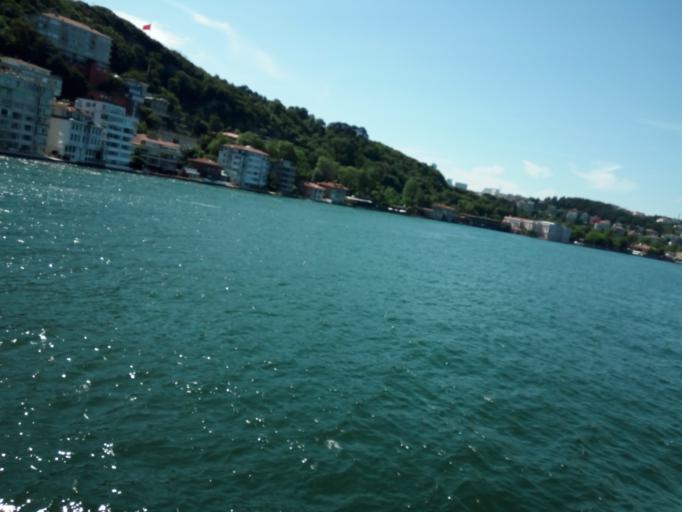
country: TR
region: Istanbul
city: UEskuedar
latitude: 41.0920
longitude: 29.0582
